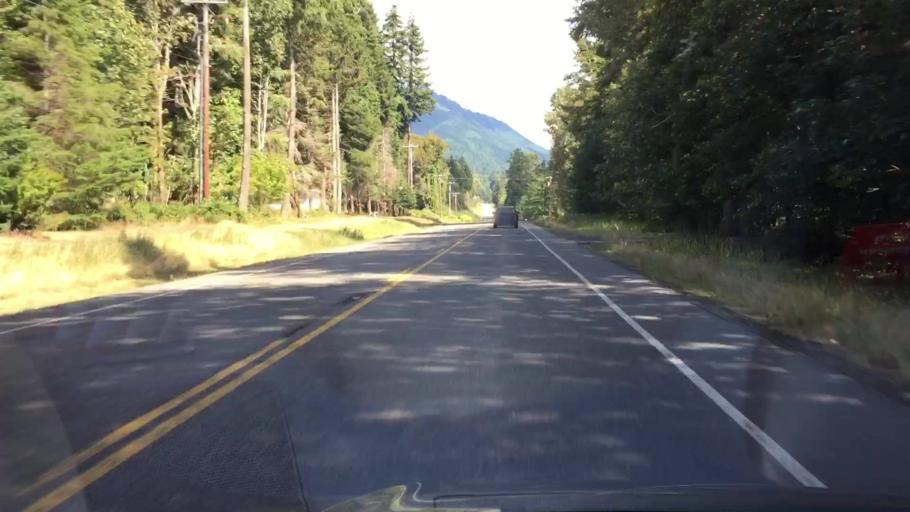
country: US
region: Washington
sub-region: Pierce County
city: Eatonville
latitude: 46.7569
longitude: -122.0055
